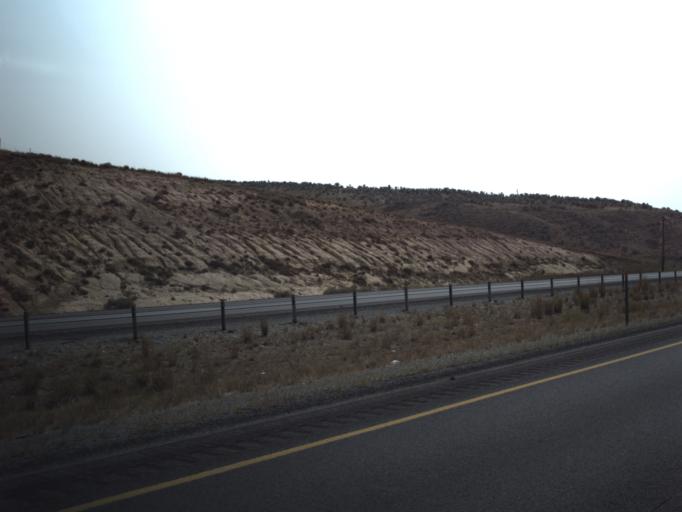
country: US
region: Wyoming
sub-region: Uinta County
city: Evanston
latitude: 41.1413
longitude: -111.1517
